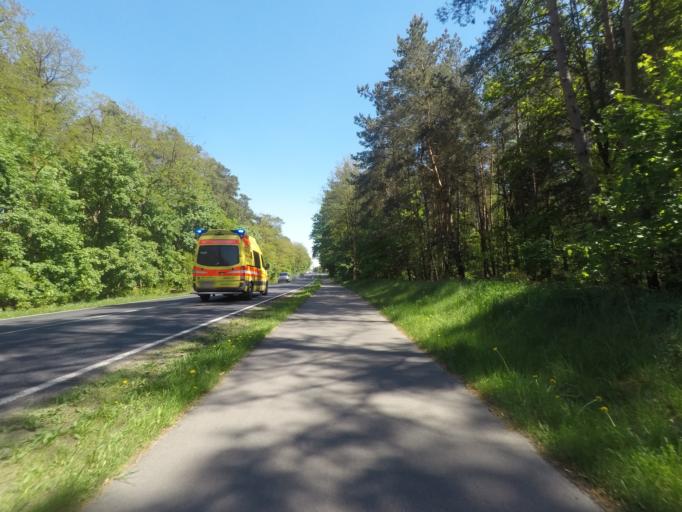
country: DE
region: Brandenburg
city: Melchow
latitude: 52.8399
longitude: 13.7119
